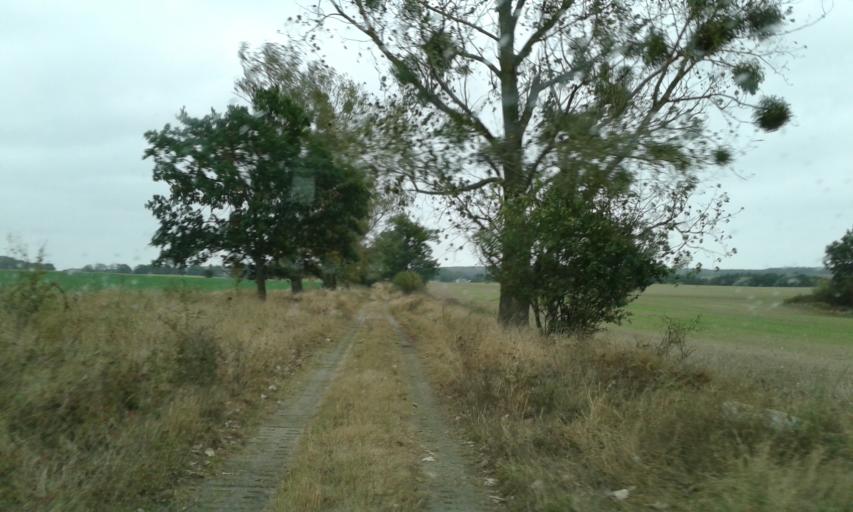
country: PL
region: West Pomeranian Voivodeship
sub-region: Powiat stargardzki
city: Dolice
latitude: 53.1111
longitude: 15.2194
